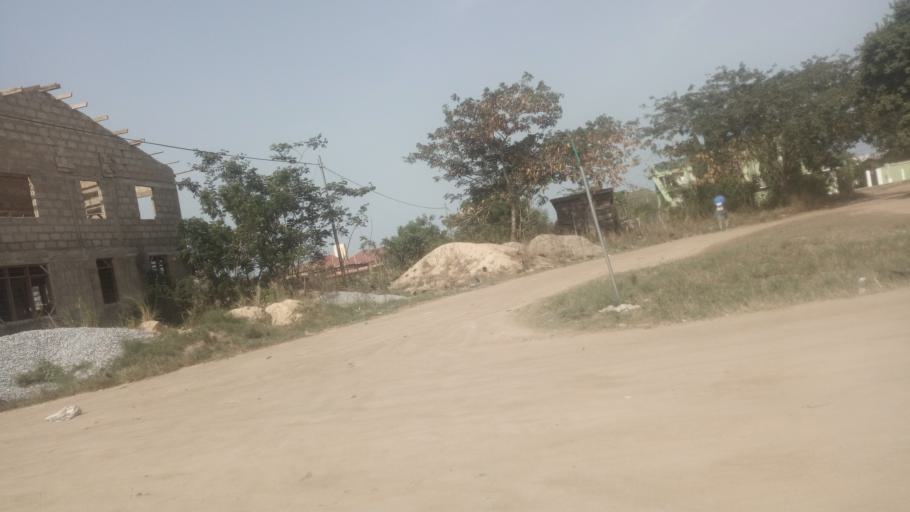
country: GH
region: Central
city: Winneba
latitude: 5.3801
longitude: -0.6441
